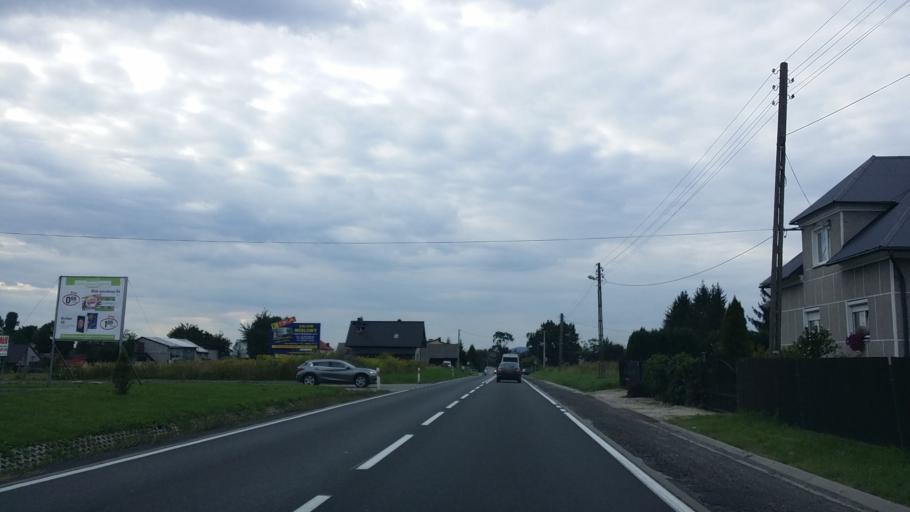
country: PL
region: Lesser Poland Voivodeship
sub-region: Powiat wadowicki
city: Spytkowice
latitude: 49.9941
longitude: 19.5159
